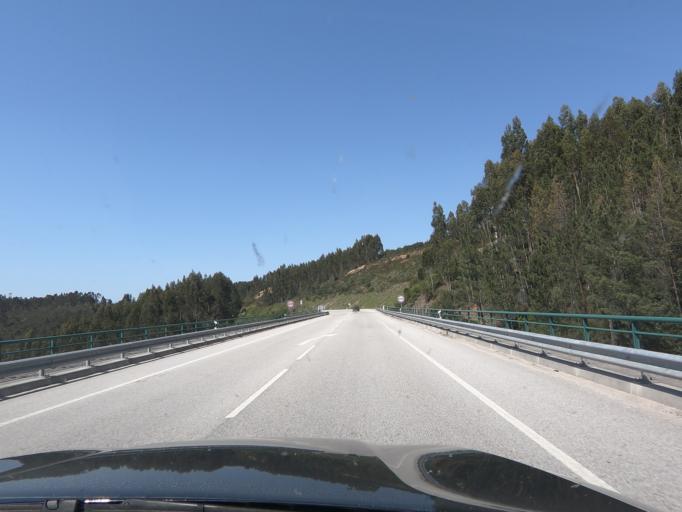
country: PT
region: Coimbra
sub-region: Lousa
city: Lousa
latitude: 40.1565
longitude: -8.2627
